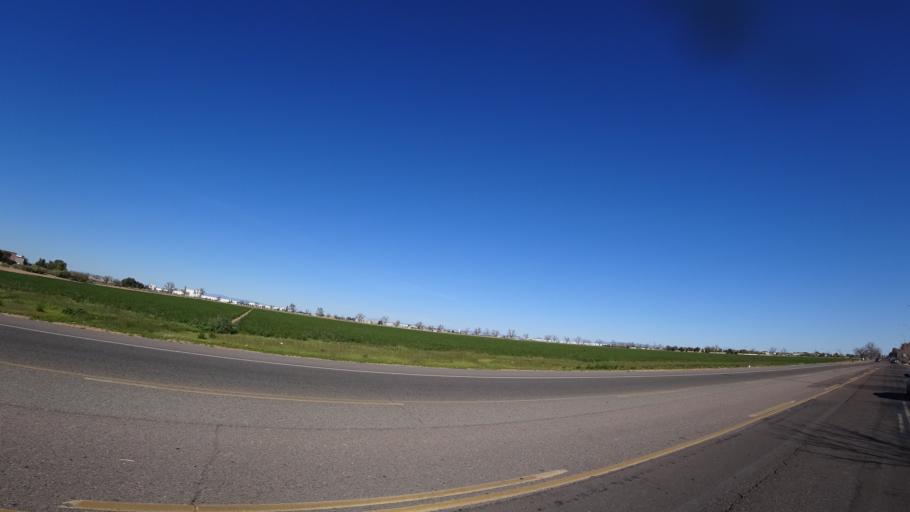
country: US
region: Arizona
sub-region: Maricopa County
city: Tolleson
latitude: 33.4211
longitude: -112.2672
